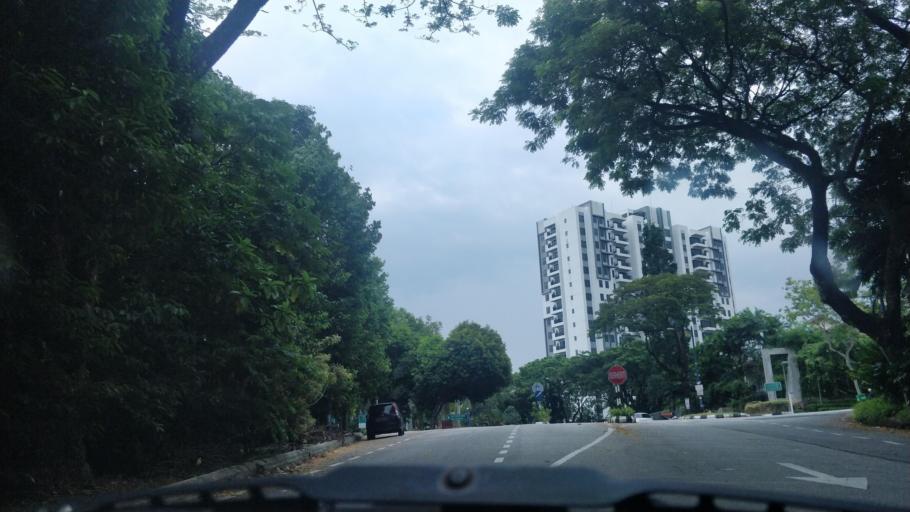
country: MY
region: Selangor
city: Kuang
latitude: 3.2084
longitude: 101.5816
